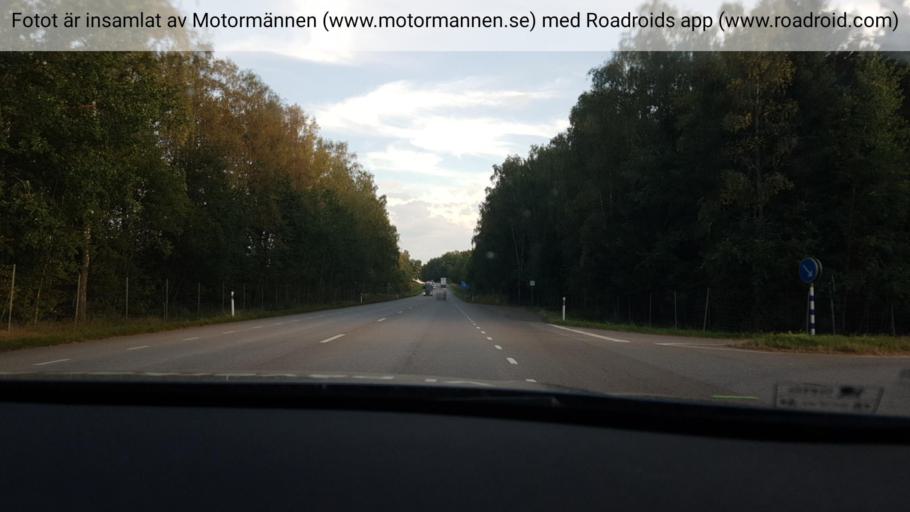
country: SE
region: Vaestra Goetaland
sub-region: Skara Kommun
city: Skara
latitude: 58.4062
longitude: 13.4629
